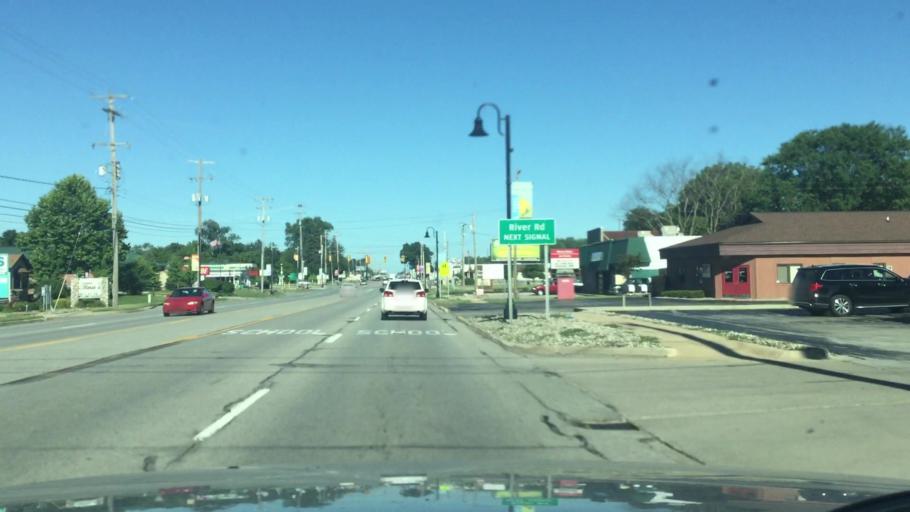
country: US
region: Michigan
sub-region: Saginaw County
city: Shields
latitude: 43.4158
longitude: -84.0497
